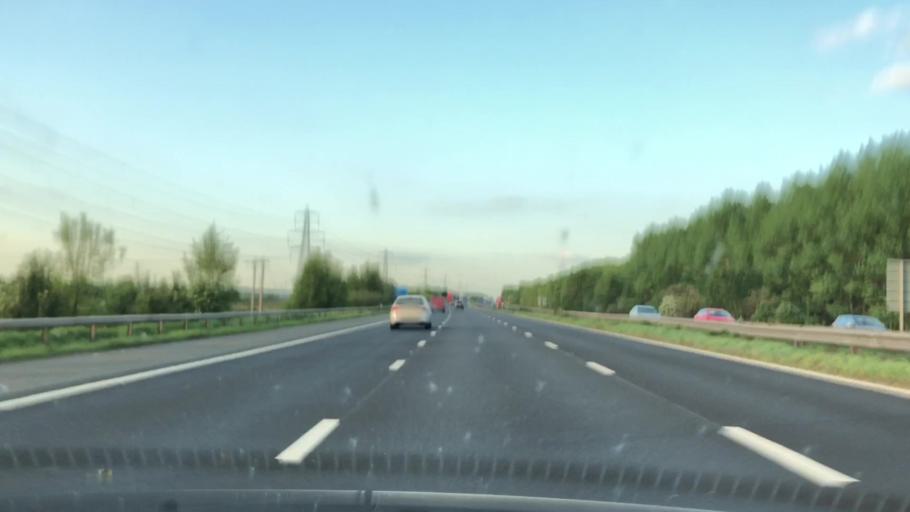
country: GB
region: England
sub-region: Cheshire West and Chester
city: Helsby
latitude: 53.2706
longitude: -2.7920
